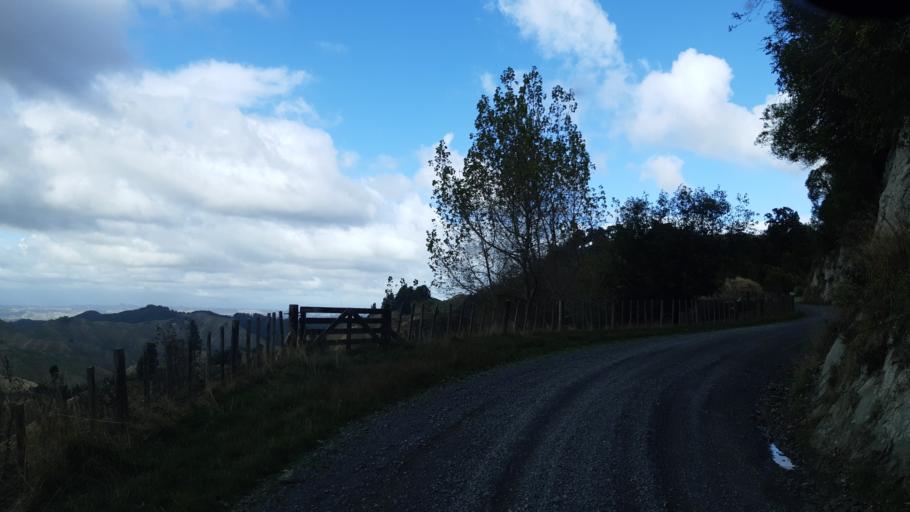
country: NZ
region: Manawatu-Wanganui
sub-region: Ruapehu District
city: Waiouru
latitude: -39.7978
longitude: 175.6721
